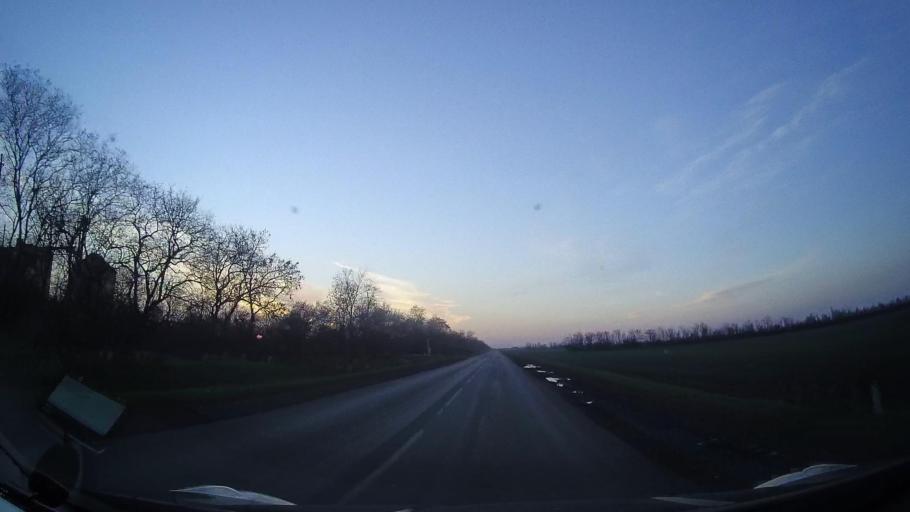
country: RU
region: Rostov
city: Zernograd
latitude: 46.9251
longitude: 40.3619
